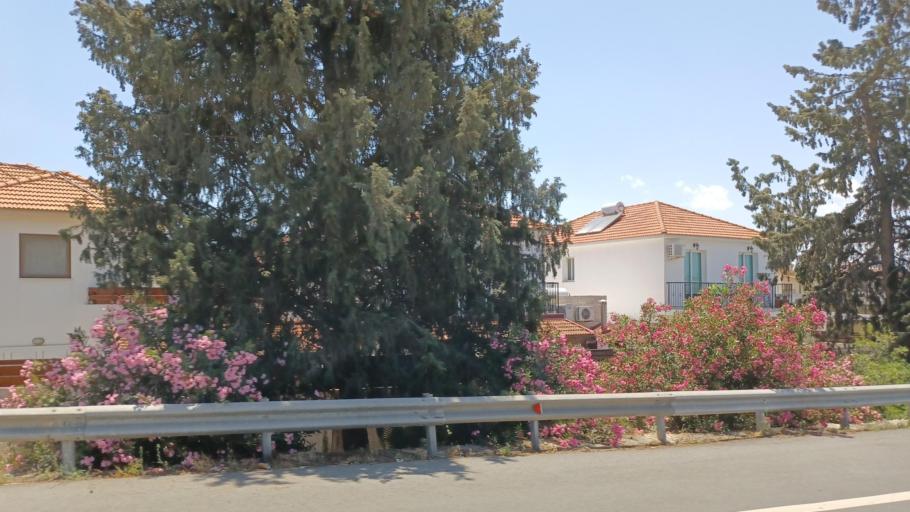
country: CY
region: Larnaka
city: Voroklini
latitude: 34.9822
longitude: 33.6777
